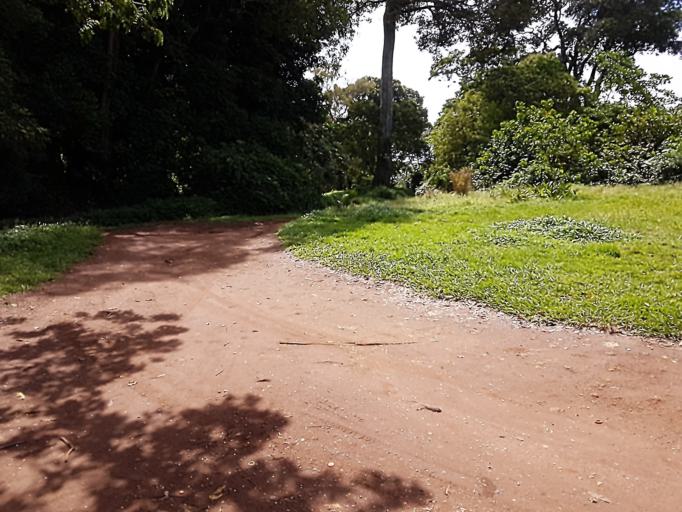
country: UG
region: Central Region
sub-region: Wakiso District
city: Entebbe
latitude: 0.0598
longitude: 32.4816
